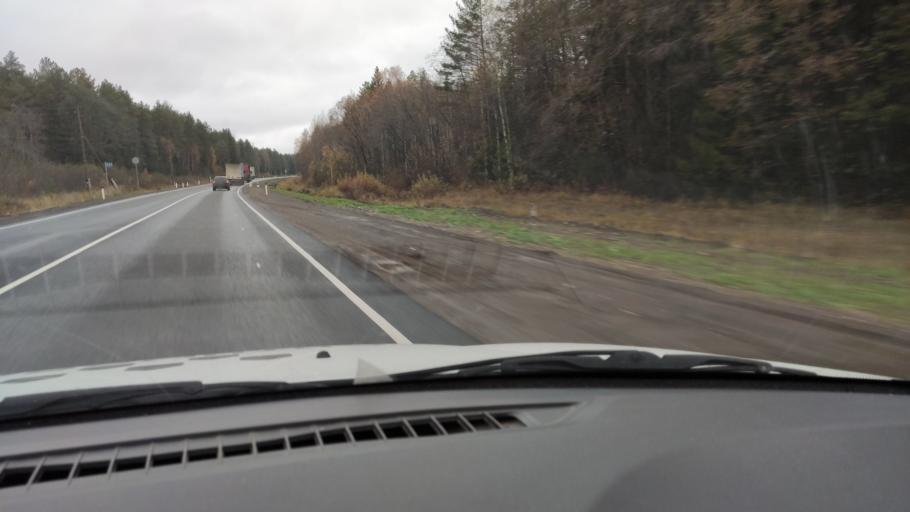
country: RU
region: Kirov
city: Belaya Kholunitsa
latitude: 58.8423
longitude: 50.7728
